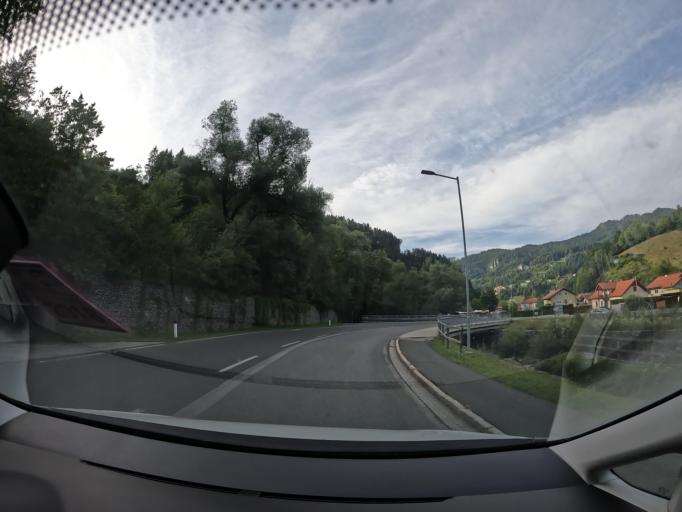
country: AT
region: Carinthia
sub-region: Politischer Bezirk Volkermarkt
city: Bad Eisenkappel
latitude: 46.4809
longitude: 14.5918
